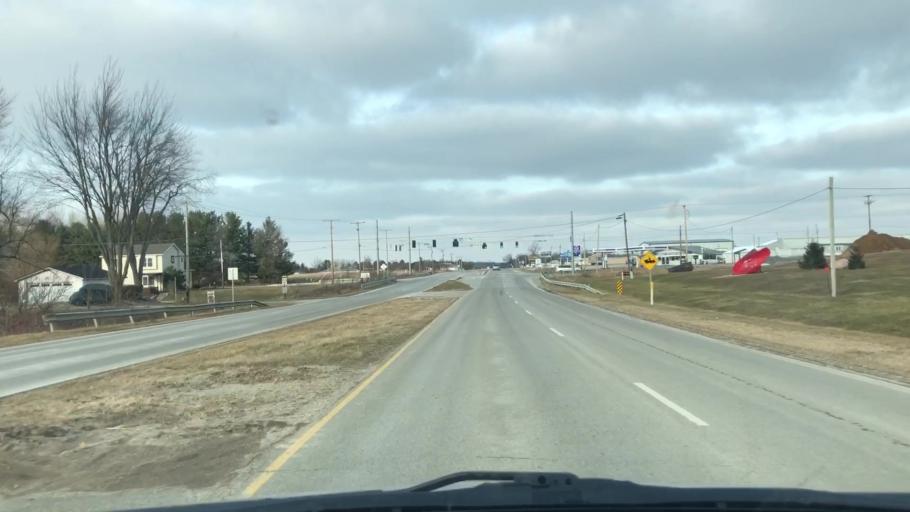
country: US
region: Indiana
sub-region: Steuben County
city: Angola
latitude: 41.6701
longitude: -85.0286
